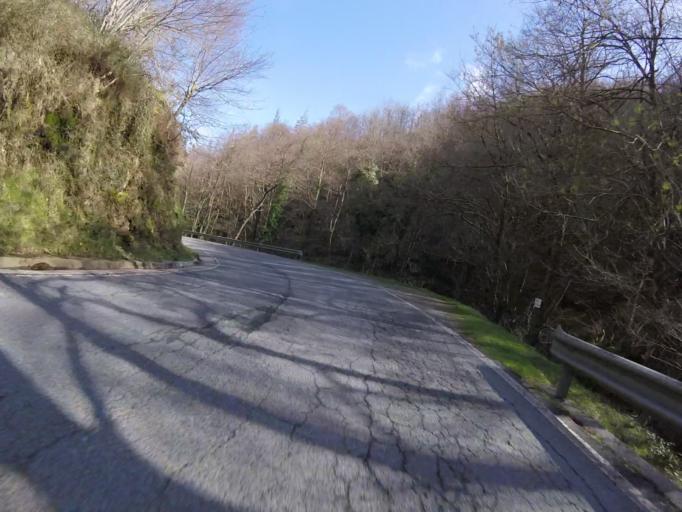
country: ES
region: Navarre
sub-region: Provincia de Navarra
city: Ezkurra
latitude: 43.0942
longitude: -1.8656
